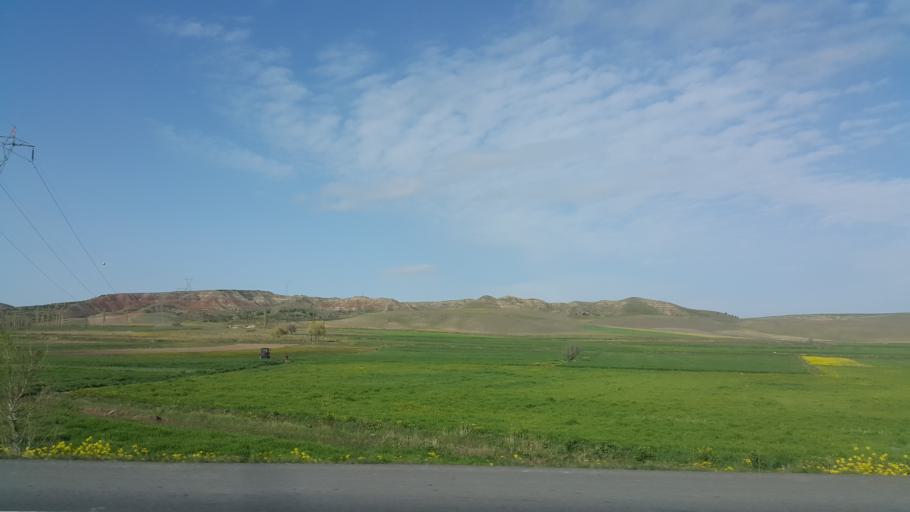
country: TR
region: Aksaray
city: Acipinar
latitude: 38.4640
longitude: 33.9131
